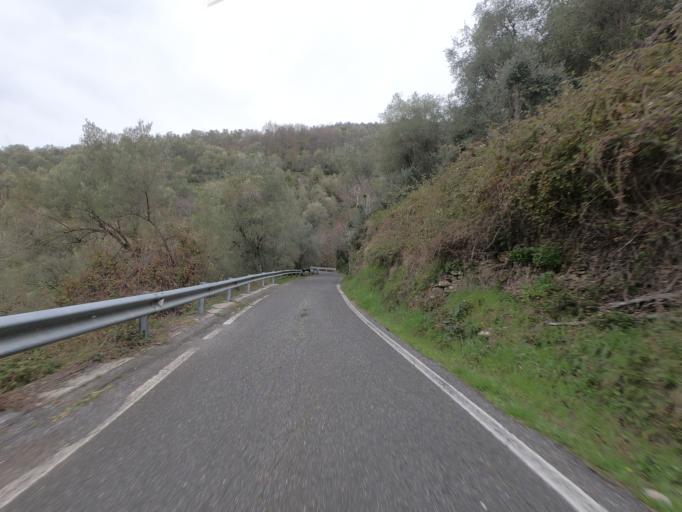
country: IT
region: Liguria
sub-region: Provincia di Savona
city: Testico
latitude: 44.0252
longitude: 8.0049
